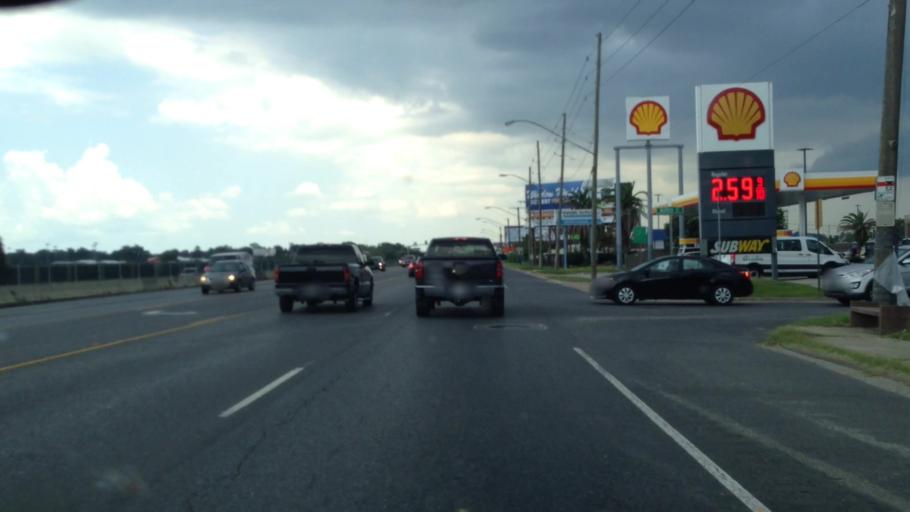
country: US
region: Louisiana
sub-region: Jefferson Parish
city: Kenner
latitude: 29.9822
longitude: -90.2567
